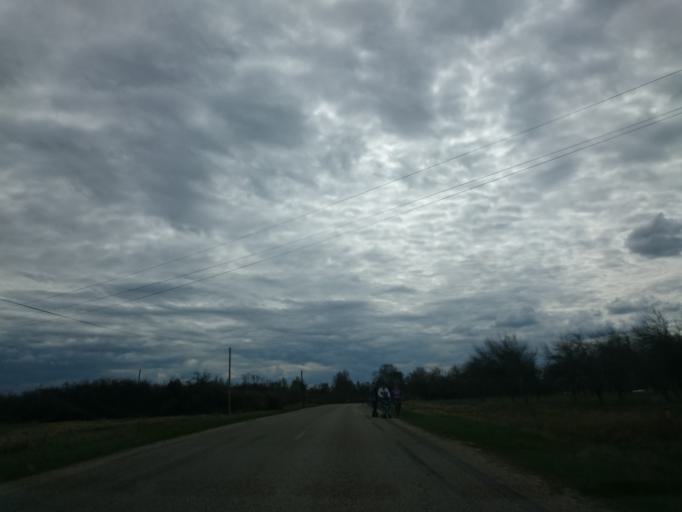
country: LV
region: Aizpute
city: Aizpute
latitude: 56.7294
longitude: 21.6078
